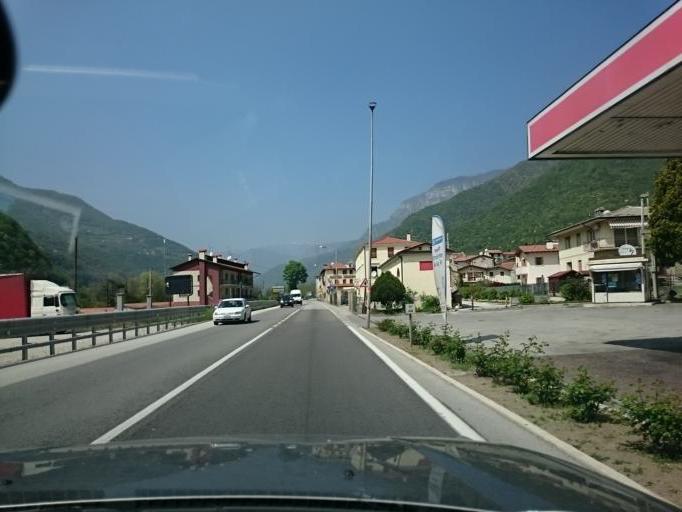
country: IT
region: Veneto
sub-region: Provincia di Vicenza
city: Solagna
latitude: 45.8186
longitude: 11.7150
